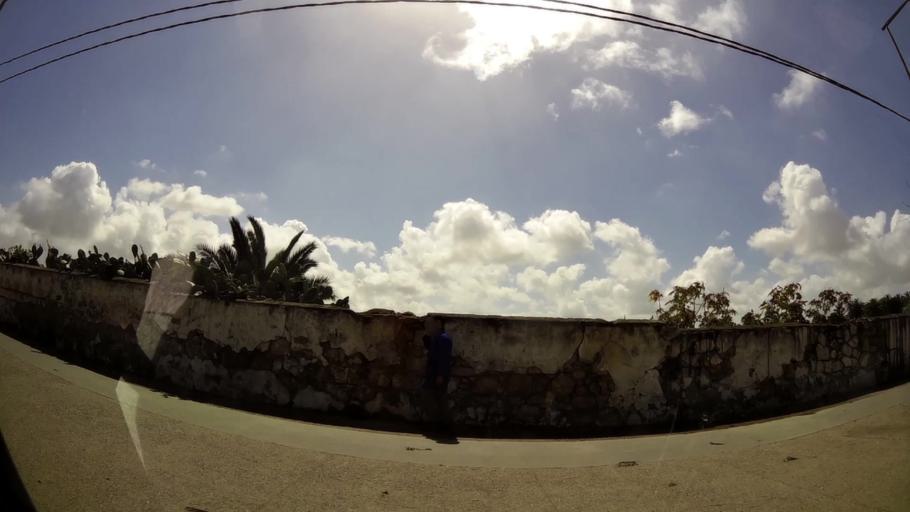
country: MA
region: Grand Casablanca
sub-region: Mediouna
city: Tit Mellil
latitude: 33.6322
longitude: -7.4707
